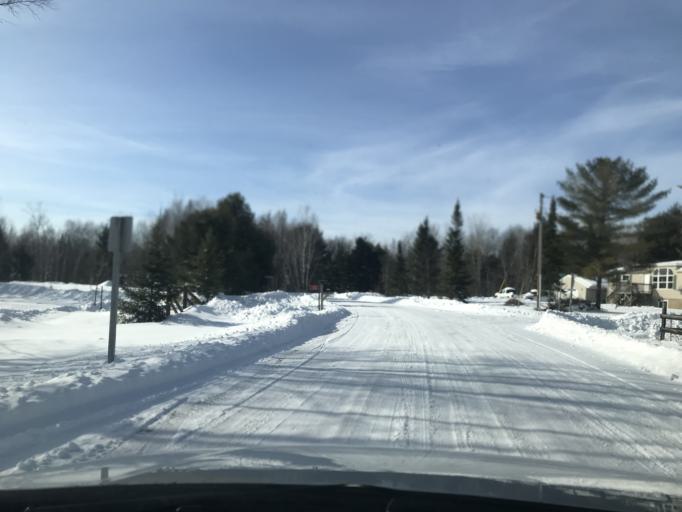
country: US
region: Wisconsin
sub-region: Oconto County
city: Gillett
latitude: 45.1504
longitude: -88.2210
